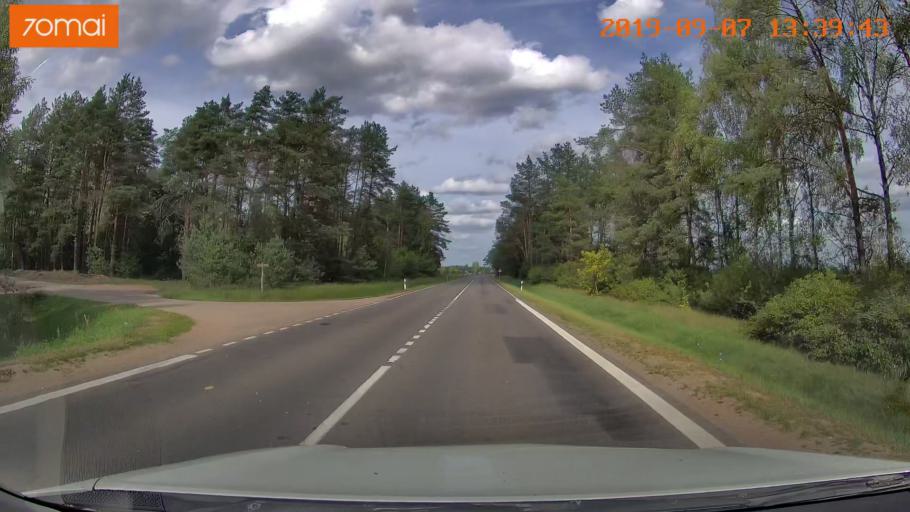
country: LT
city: Skaidiskes
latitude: 54.5724
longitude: 25.3159
